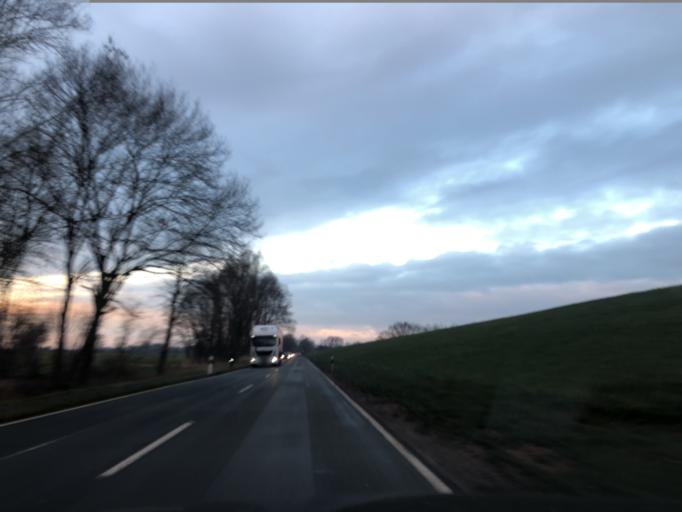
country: DE
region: Lower Saxony
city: Lemwerder
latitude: 53.1216
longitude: 8.6381
